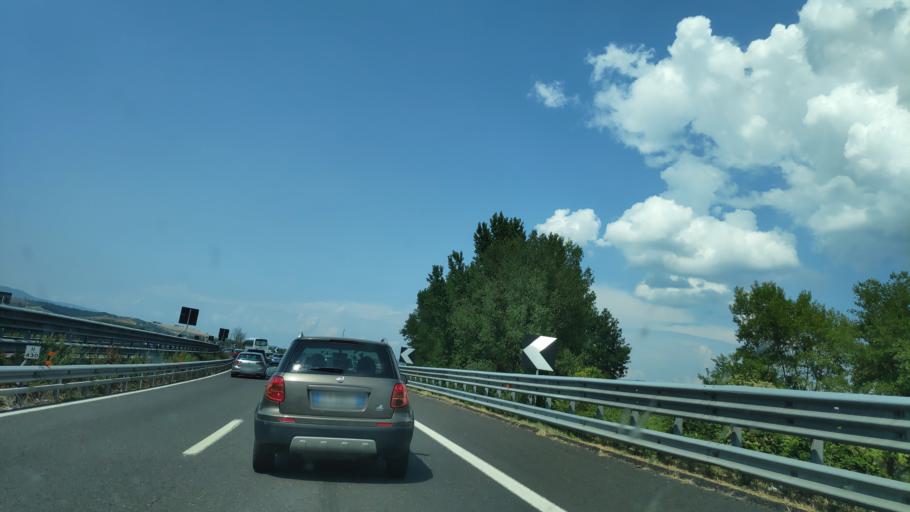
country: IT
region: Umbria
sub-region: Provincia di Terni
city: Fabro Scalo
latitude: 42.8607
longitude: 12.0378
